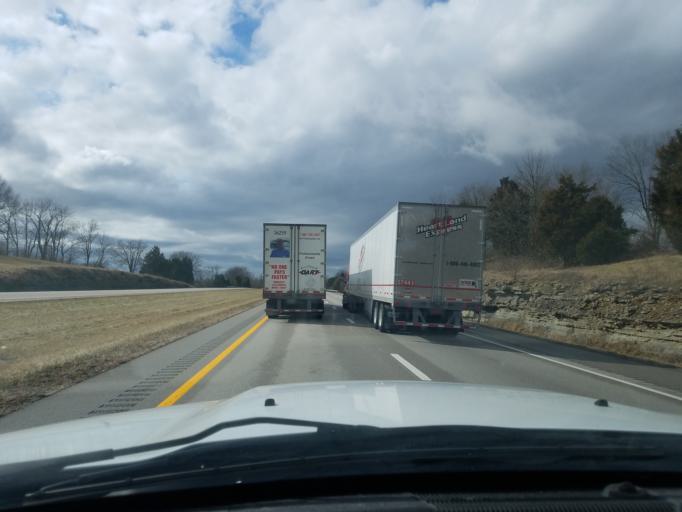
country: US
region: Kentucky
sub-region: Montgomery County
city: Mount Sterling
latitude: 38.0944
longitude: -83.8694
